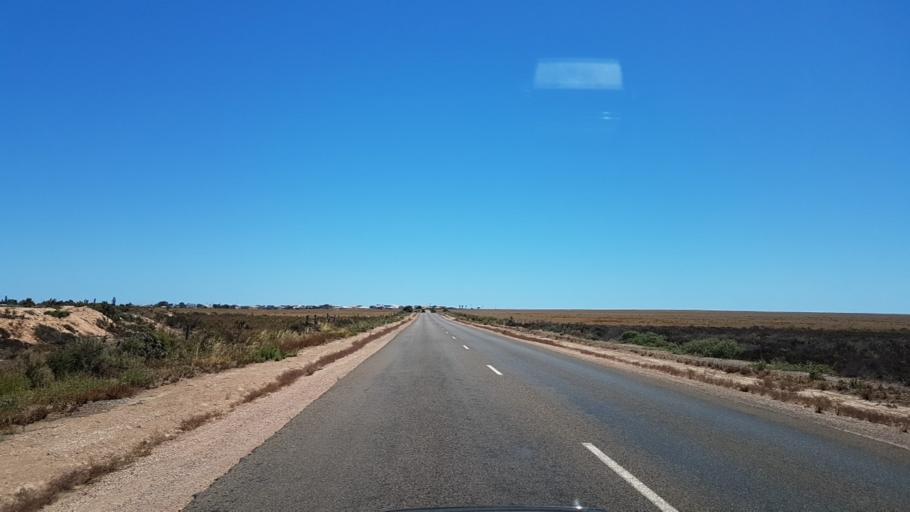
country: AU
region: South Australia
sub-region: Copper Coast
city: Wallaroo
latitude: -33.9063
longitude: 137.6397
